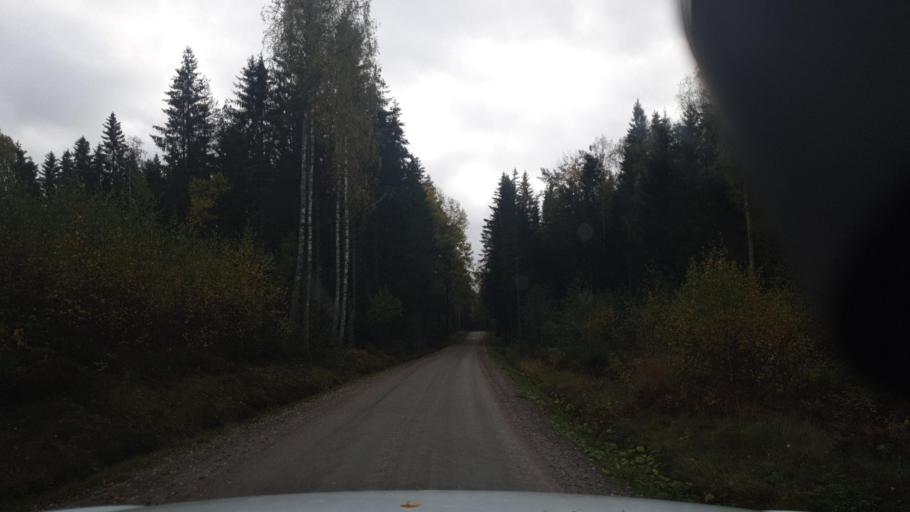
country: SE
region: Vaermland
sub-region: Karlstads Kommun
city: Edsvalla
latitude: 59.5178
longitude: 13.0097
